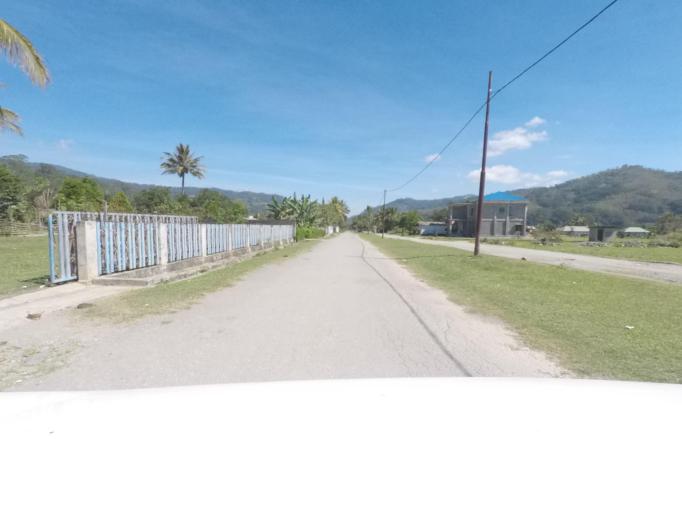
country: TL
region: Ermera
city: Gleno
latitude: -8.7227
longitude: 125.4307
